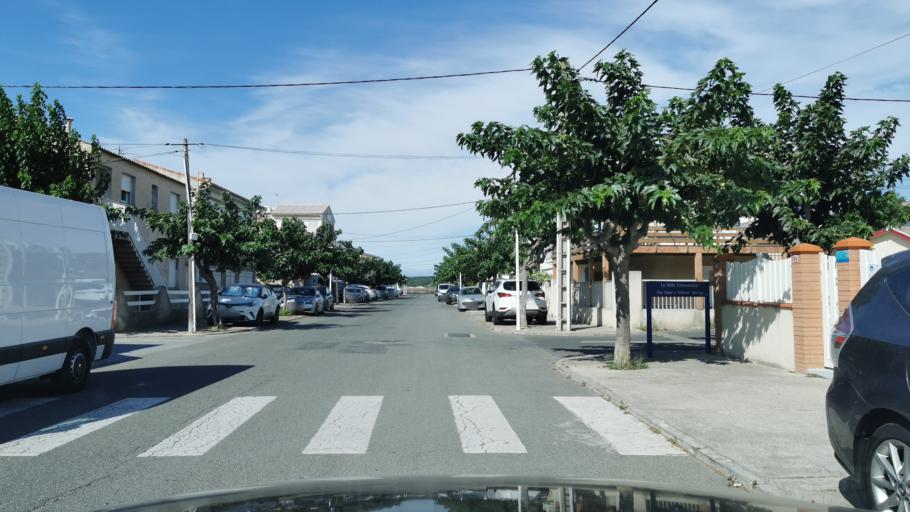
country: FR
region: Languedoc-Roussillon
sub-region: Departement de l'Aude
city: Gruissan
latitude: 43.0975
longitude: 3.1086
